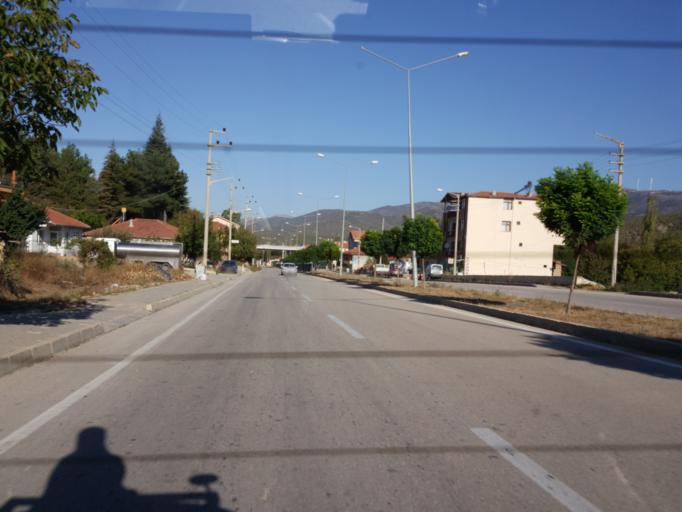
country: TR
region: Amasya
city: Ezinepazari
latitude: 40.5689
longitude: 36.1386
